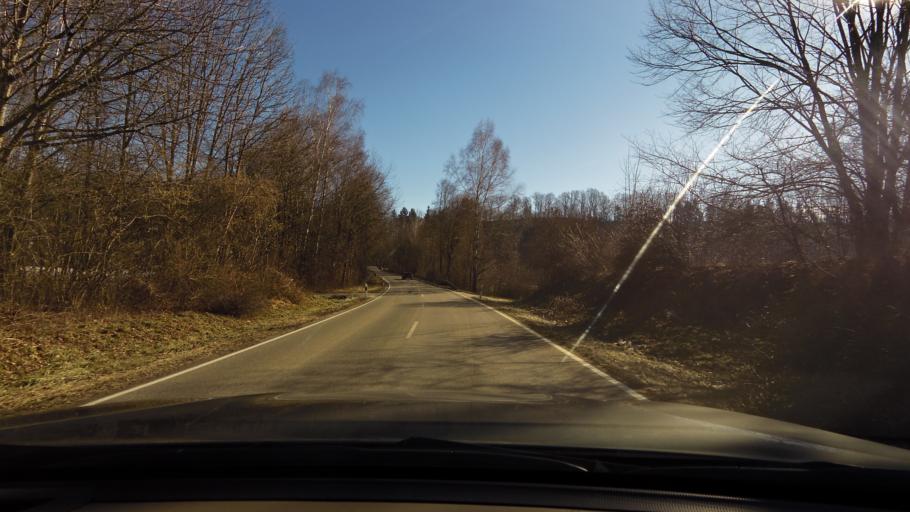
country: DE
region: Bavaria
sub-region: Upper Bavaria
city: Kraiburg am Inn
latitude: 48.1878
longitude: 12.4430
